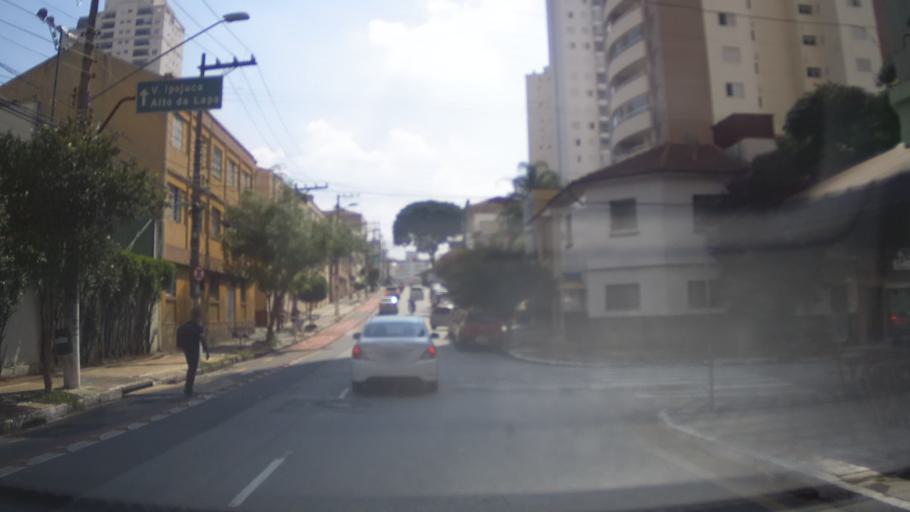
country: BR
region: Sao Paulo
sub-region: Sao Paulo
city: Sao Paulo
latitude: -23.5260
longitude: -46.6990
